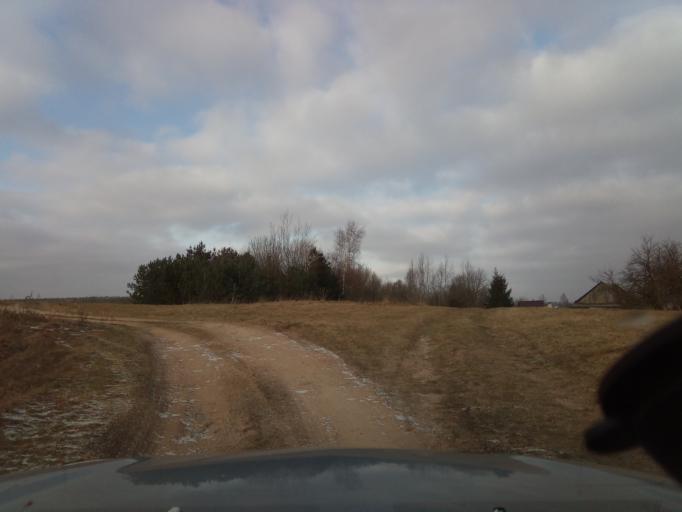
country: LT
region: Alytaus apskritis
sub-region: Alytaus rajonas
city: Daugai
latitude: 54.3786
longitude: 24.4162
